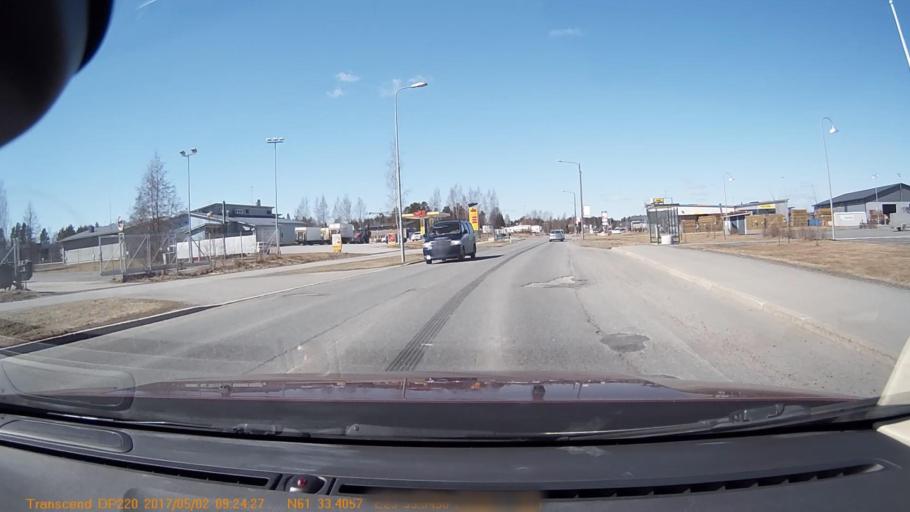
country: FI
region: Pirkanmaa
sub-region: Tampere
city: Yloejaervi
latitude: 61.5568
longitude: 23.5654
